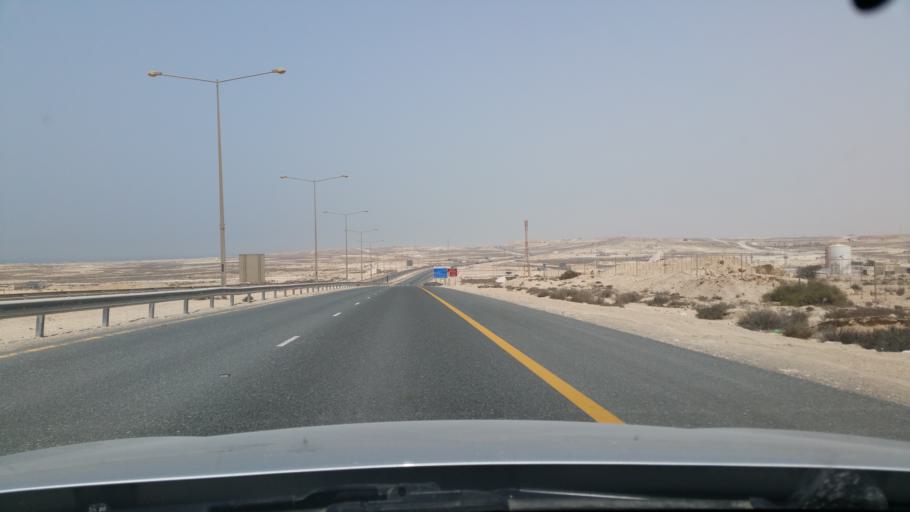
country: QA
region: Baladiyat ar Rayyan
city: Dukhan
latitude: 25.3309
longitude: 50.7852
